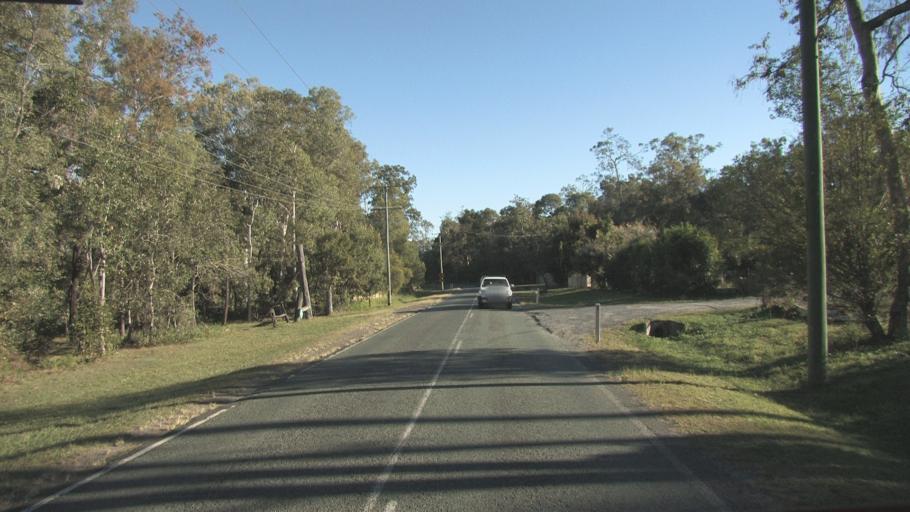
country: AU
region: Queensland
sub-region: Logan
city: Chambers Flat
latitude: -27.7541
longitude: 153.0508
